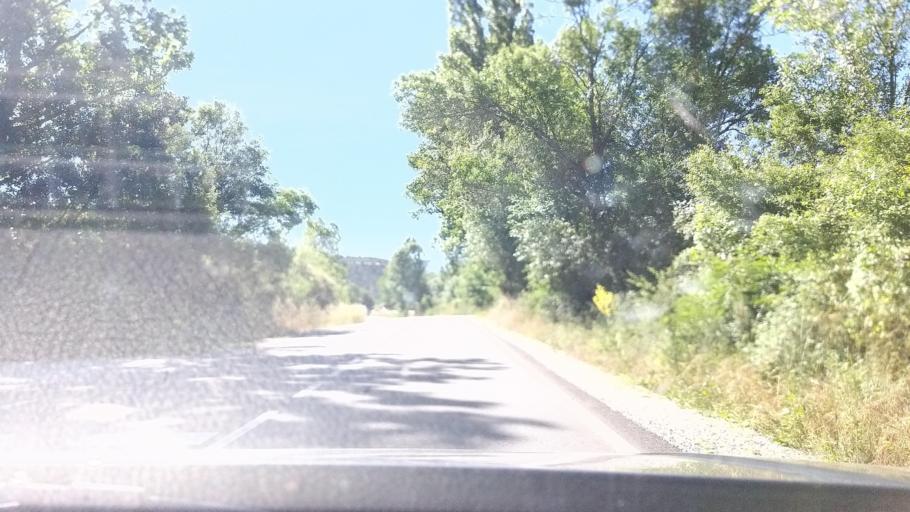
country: ES
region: Castille and Leon
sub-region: Provincia de Segovia
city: Pedraza
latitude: 41.1412
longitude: -3.8232
